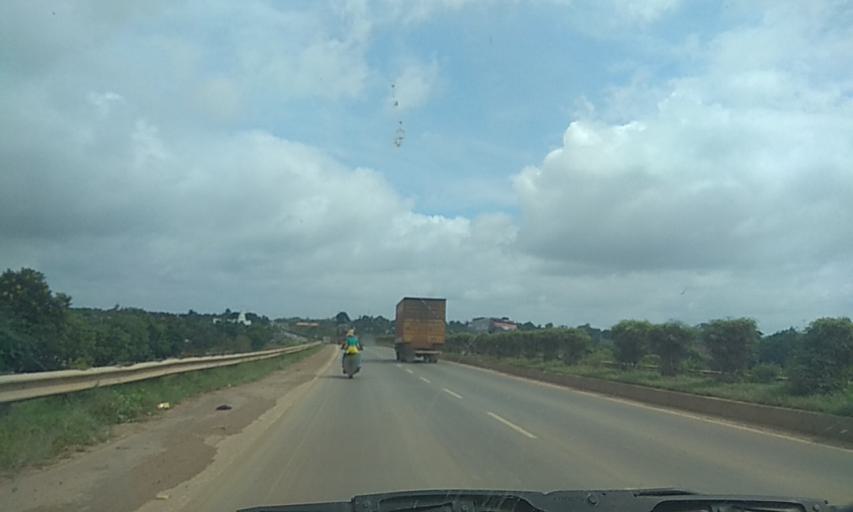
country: IN
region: Karnataka
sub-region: Dharwad
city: Kundgol
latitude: 15.2180
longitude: 75.1404
